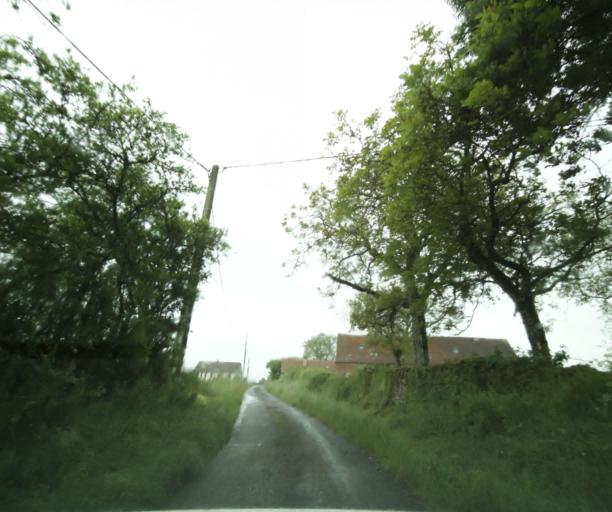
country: FR
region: Bourgogne
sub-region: Departement de Saone-et-Loire
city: Ciry-le-Noble
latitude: 46.5383
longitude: 4.3586
